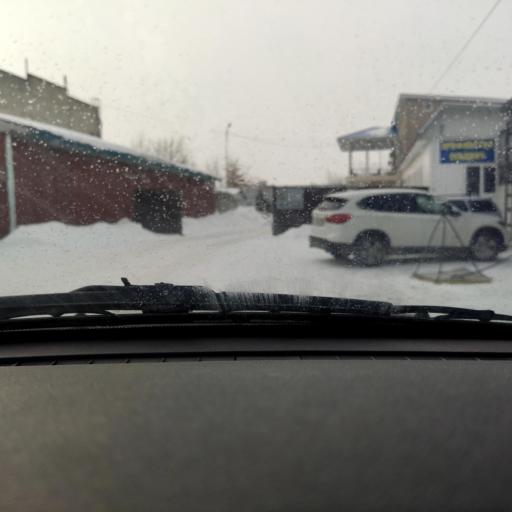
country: RU
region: Samara
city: Tol'yatti
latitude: 53.5505
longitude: 49.4420
